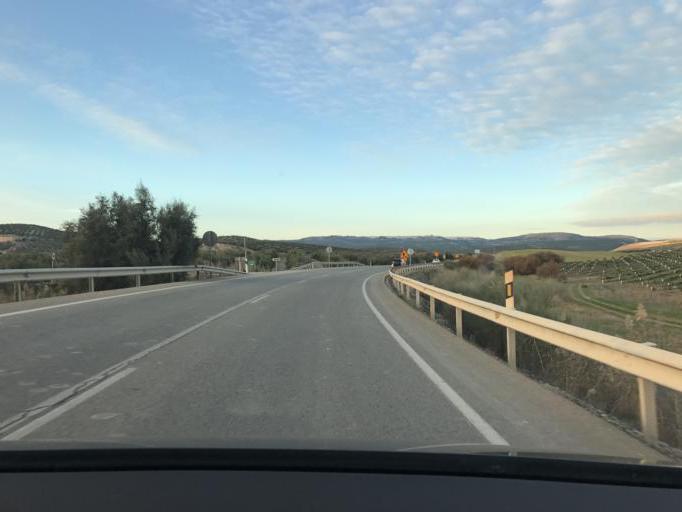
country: ES
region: Andalusia
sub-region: Provincia de Jaen
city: Ubeda
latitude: 37.9435
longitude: -3.3597
